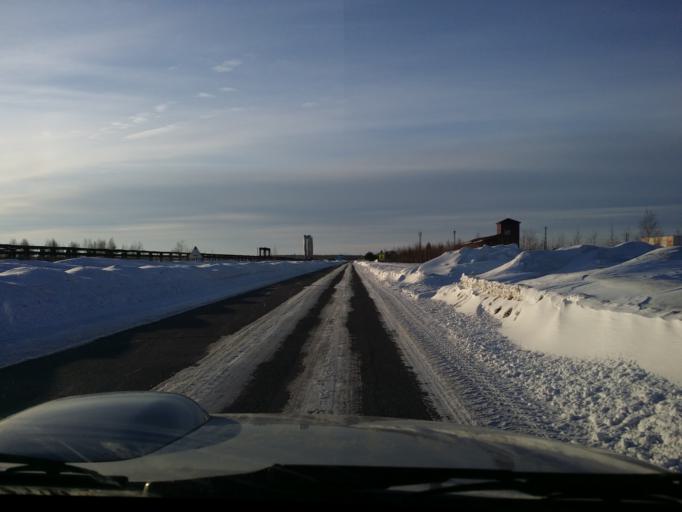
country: RU
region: Khanty-Mansiyskiy Avtonomnyy Okrug
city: Izluchinsk
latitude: 60.9770
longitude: 76.9278
